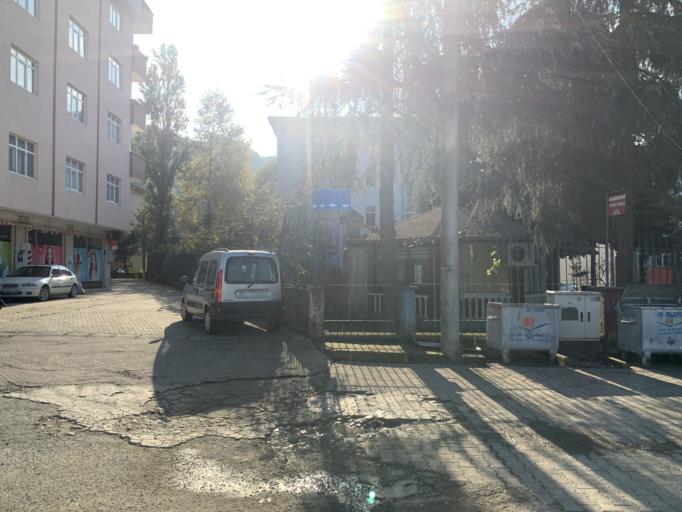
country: TR
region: Trabzon
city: Of
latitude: 40.9399
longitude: 40.2704
